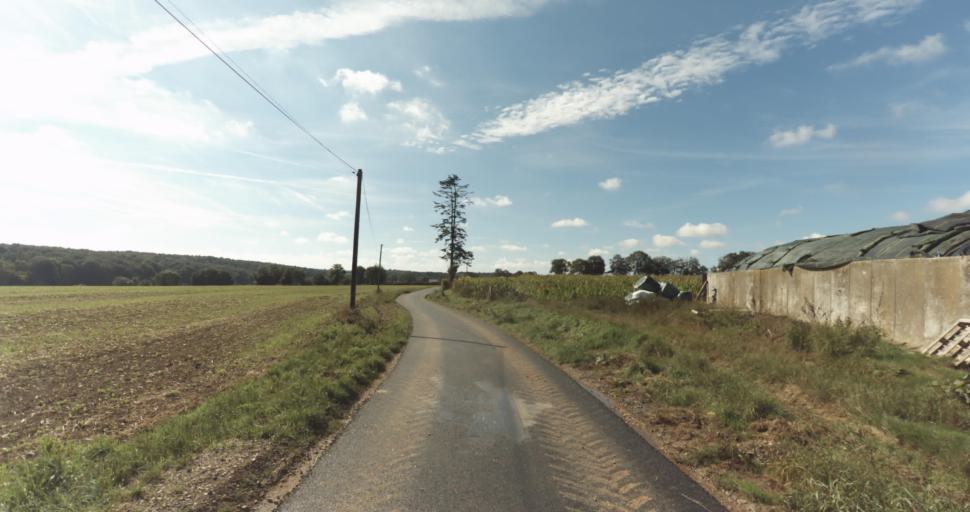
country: FR
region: Lower Normandy
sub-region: Departement du Calvados
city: Orbec
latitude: 48.9426
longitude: 0.3626
